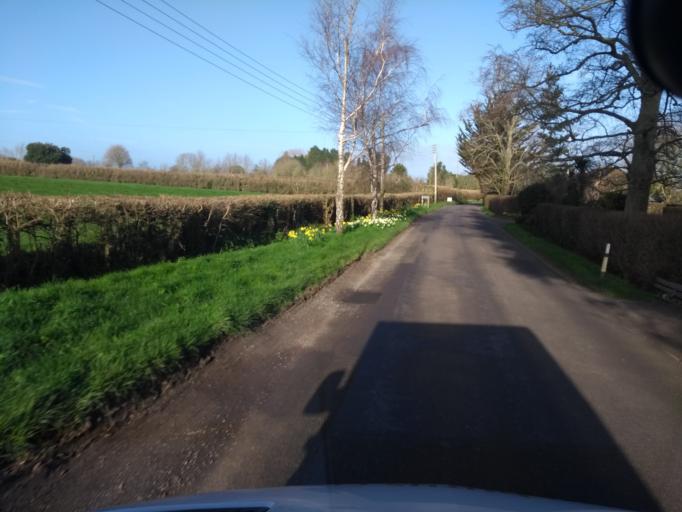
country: GB
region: England
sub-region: Somerset
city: Woolavington
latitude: 51.1483
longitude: -2.8709
